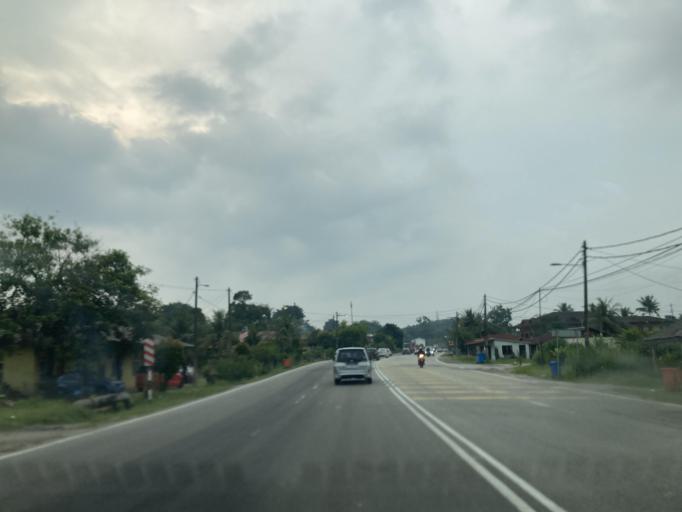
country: MY
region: Selangor
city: Kuang
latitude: 3.2143
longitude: 101.5342
